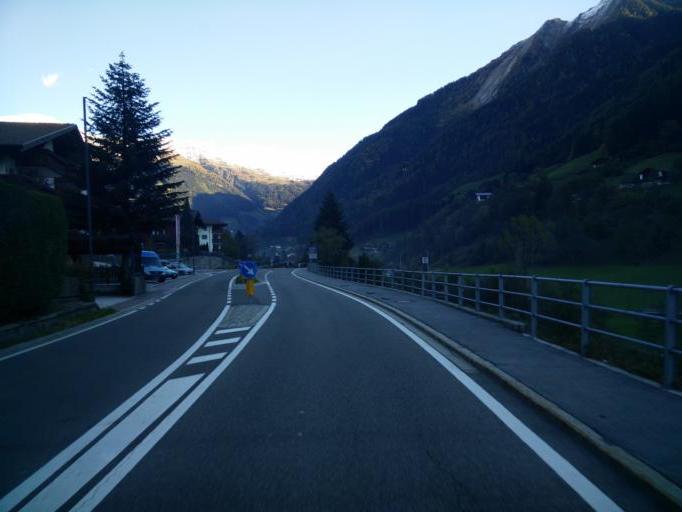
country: IT
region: Trentino-Alto Adige
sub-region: Bolzano
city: San Martino in Passiria
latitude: 46.7791
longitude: 11.2251
